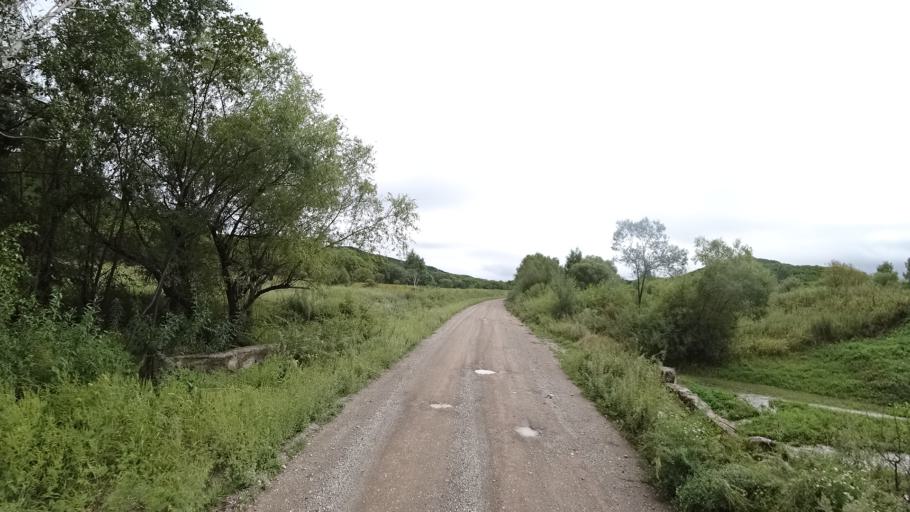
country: RU
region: Primorskiy
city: Monastyrishche
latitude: 44.1671
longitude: 132.5312
